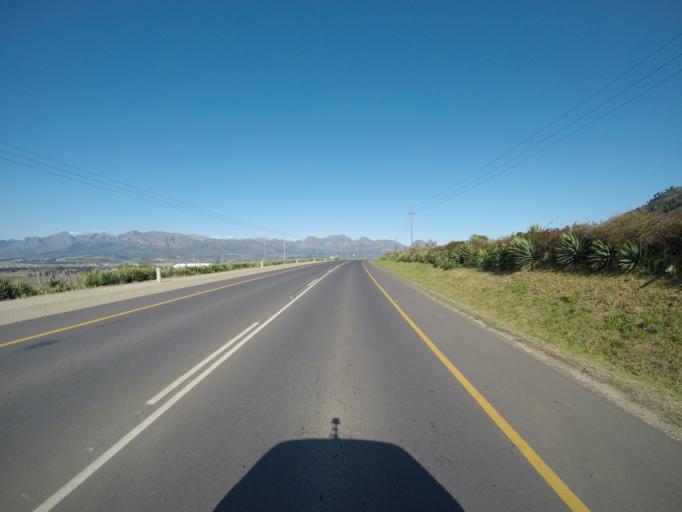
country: ZA
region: Western Cape
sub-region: Cape Winelands District Municipality
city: Noorder-Paarl
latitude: -33.6794
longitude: 18.9431
